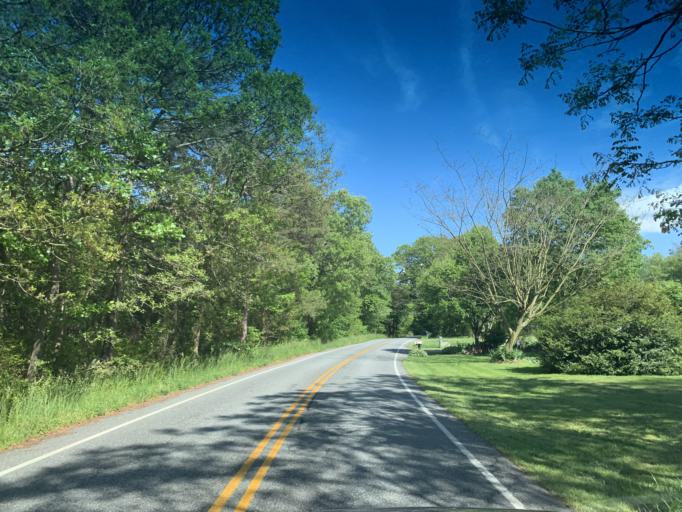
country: US
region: Maryland
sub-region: Cecil County
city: Rising Sun
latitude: 39.7202
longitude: -76.1705
